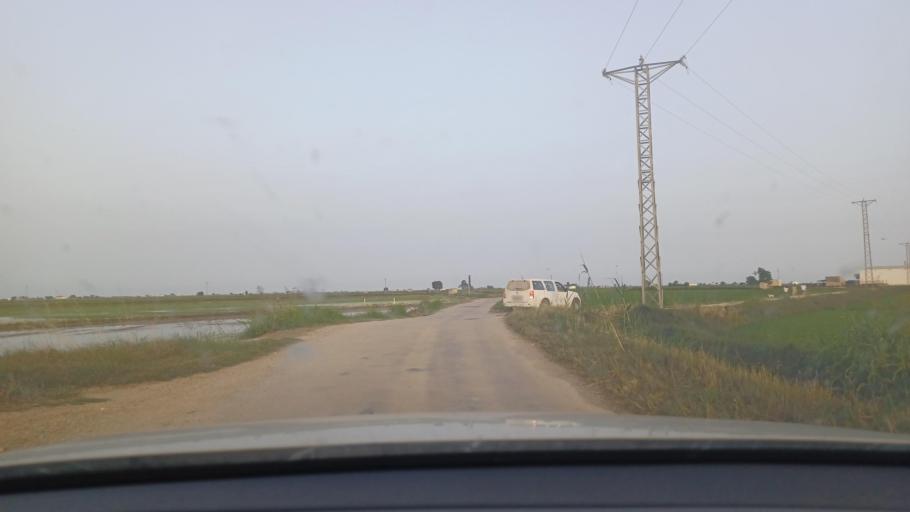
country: ES
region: Catalonia
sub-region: Provincia de Tarragona
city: Amposta
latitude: 40.7024
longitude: 0.6382
